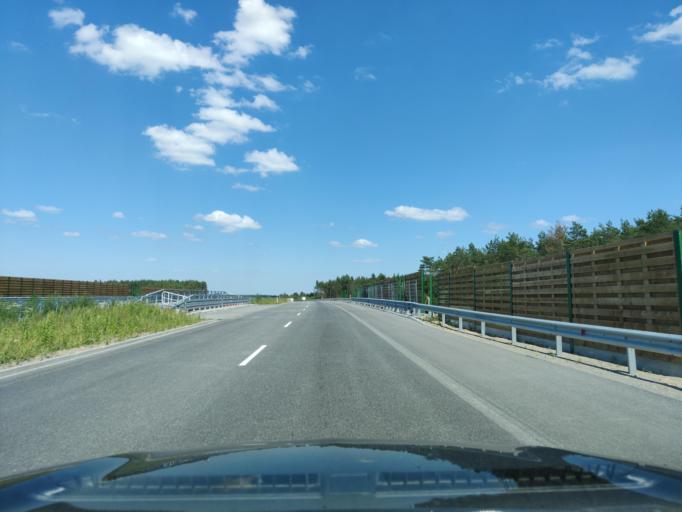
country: PL
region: Masovian Voivodeship
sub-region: Powiat mlawski
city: Wisniewo
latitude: 52.9793
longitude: 20.3362
